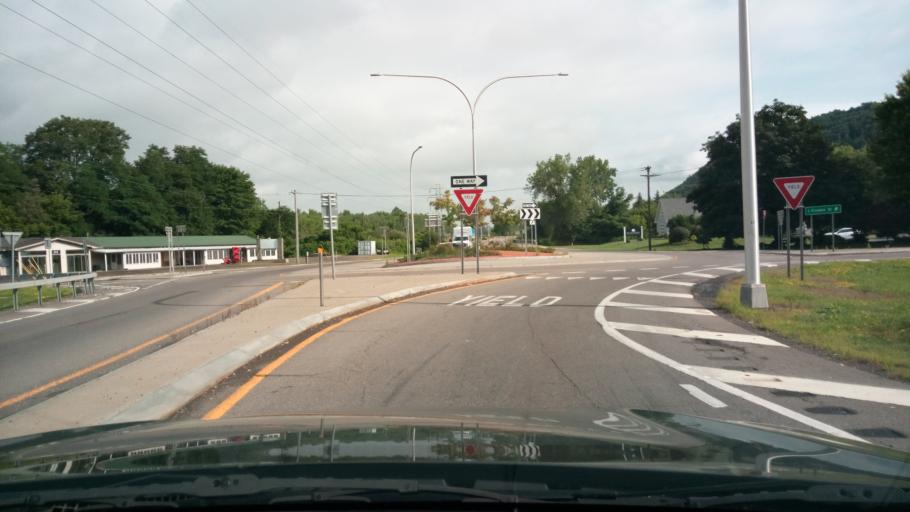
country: US
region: New York
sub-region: Chemung County
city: Horseheads
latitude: 42.1672
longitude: -76.8055
